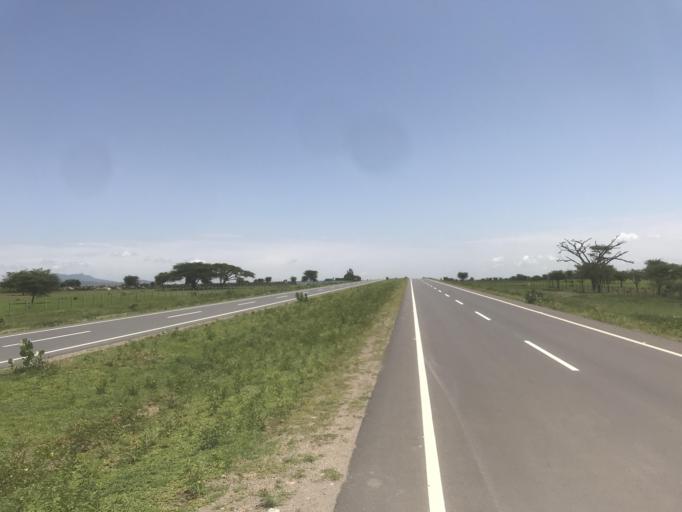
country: ET
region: Oromiya
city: Mojo
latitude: 8.3659
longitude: 38.9934
